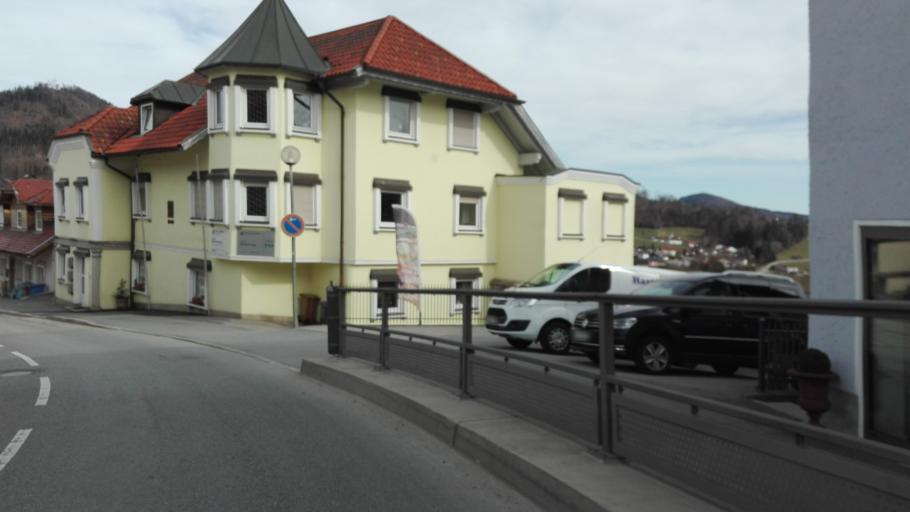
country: DE
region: Bavaria
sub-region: Lower Bavaria
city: Hauzenberg
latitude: 48.6476
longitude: 13.6243
